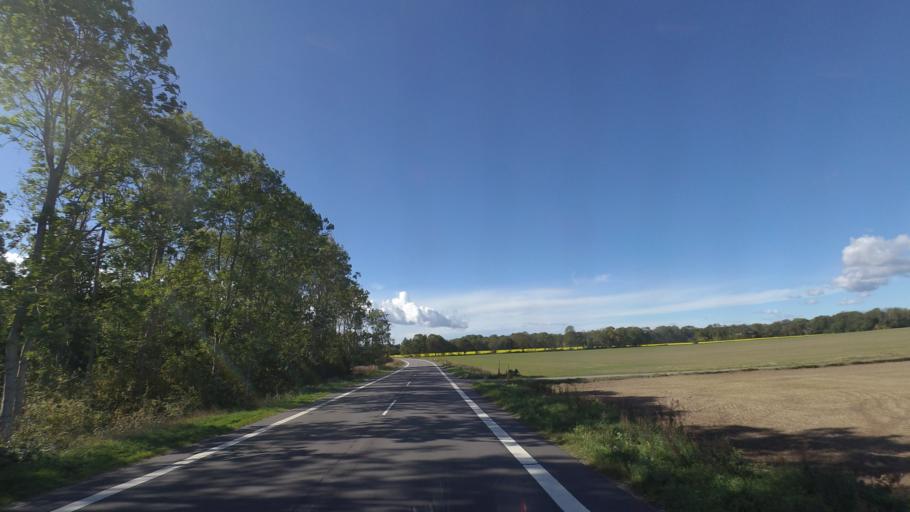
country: DK
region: Capital Region
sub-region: Bornholm Kommune
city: Akirkeby
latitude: 55.0690
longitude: 14.9853
